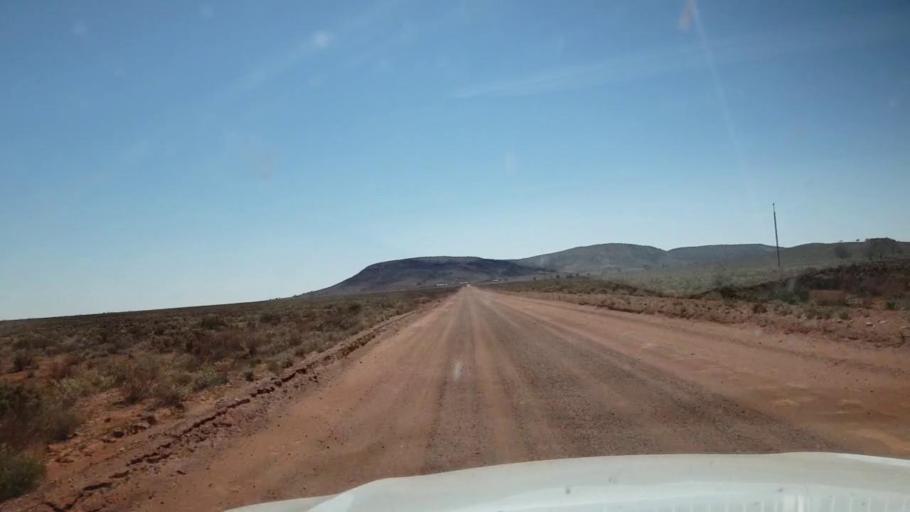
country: AU
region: South Australia
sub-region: Whyalla
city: Whyalla
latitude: -32.7043
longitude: 137.1365
